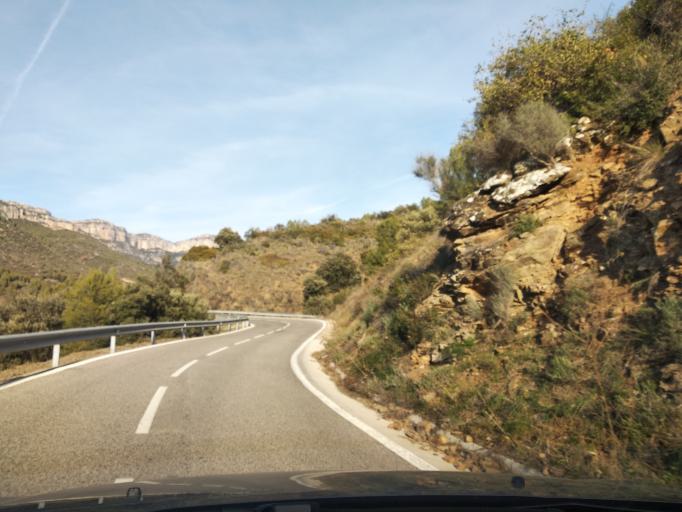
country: ES
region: Catalonia
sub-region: Provincia de Tarragona
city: Margalef
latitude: 41.2407
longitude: 0.7888
